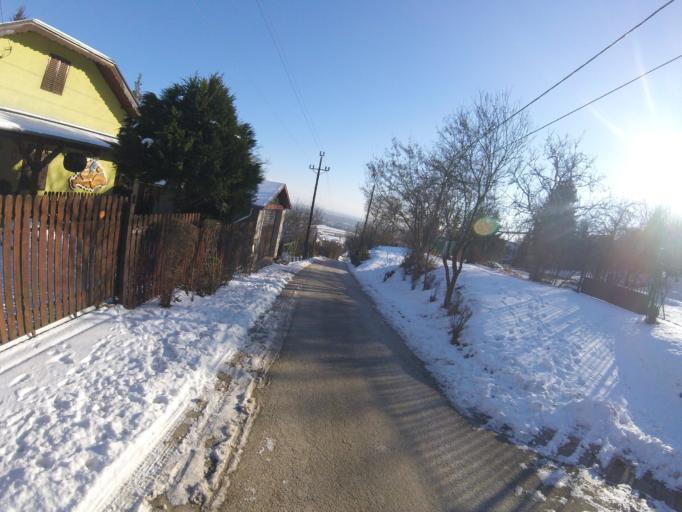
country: HU
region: Pest
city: Kismaros
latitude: 47.8343
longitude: 18.9994
